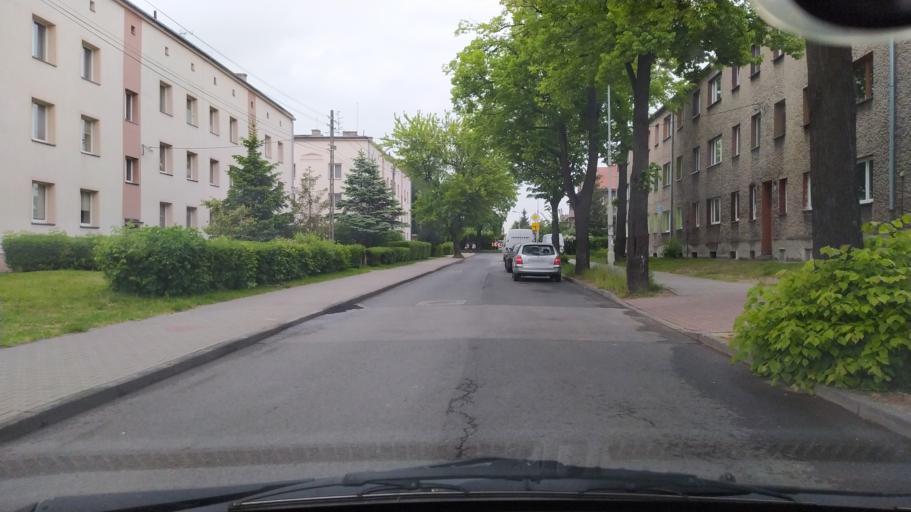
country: PL
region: Silesian Voivodeship
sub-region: Powiat gliwicki
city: Przyszowice
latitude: 50.2918
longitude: 18.7401
